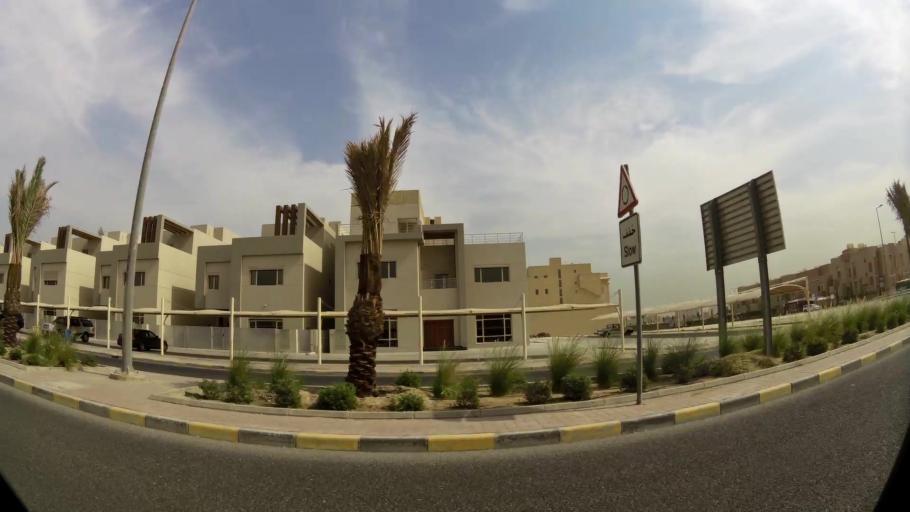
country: KW
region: Al Farwaniyah
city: Janub as Surrah
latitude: 29.2909
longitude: 47.9927
